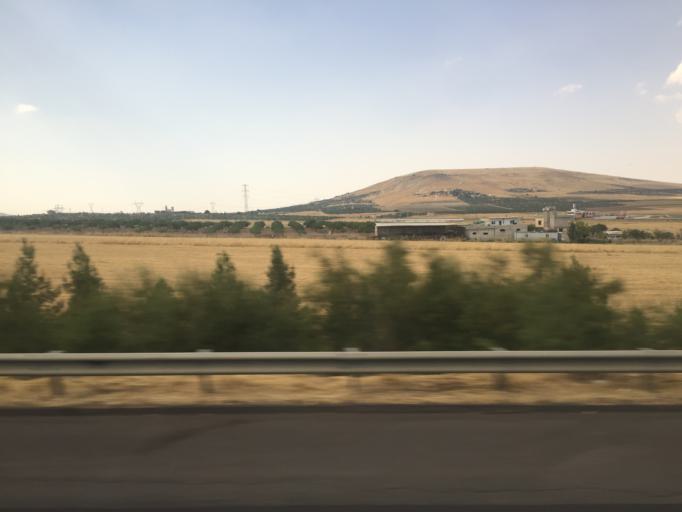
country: TR
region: Sanliurfa
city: Akziyaret
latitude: 37.2630
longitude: 38.7608
